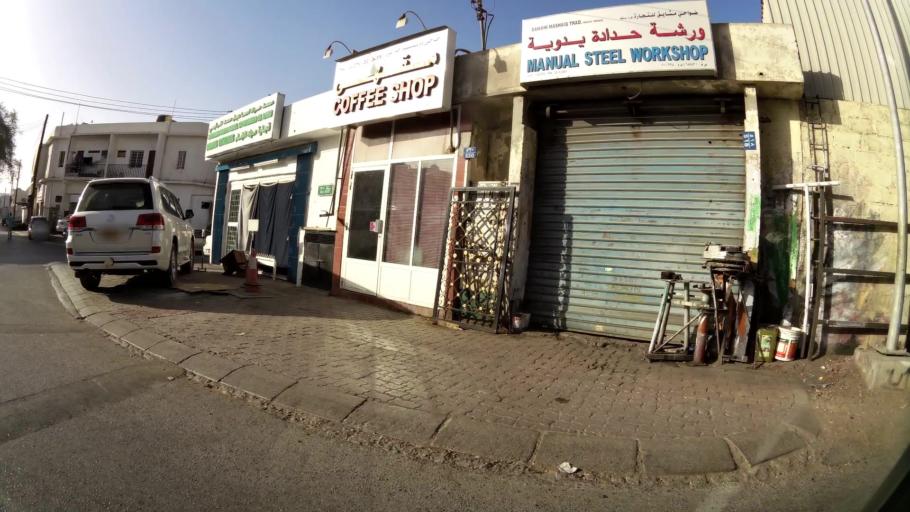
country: OM
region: Muhafazat Masqat
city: Muscat
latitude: 23.5863
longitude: 58.5528
